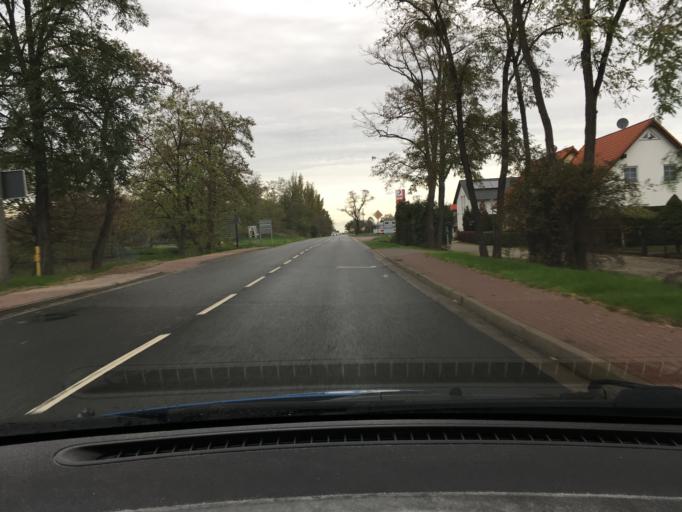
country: DE
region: Saxony-Anhalt
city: Zerbst
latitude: 51.9738
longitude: 12.0670
